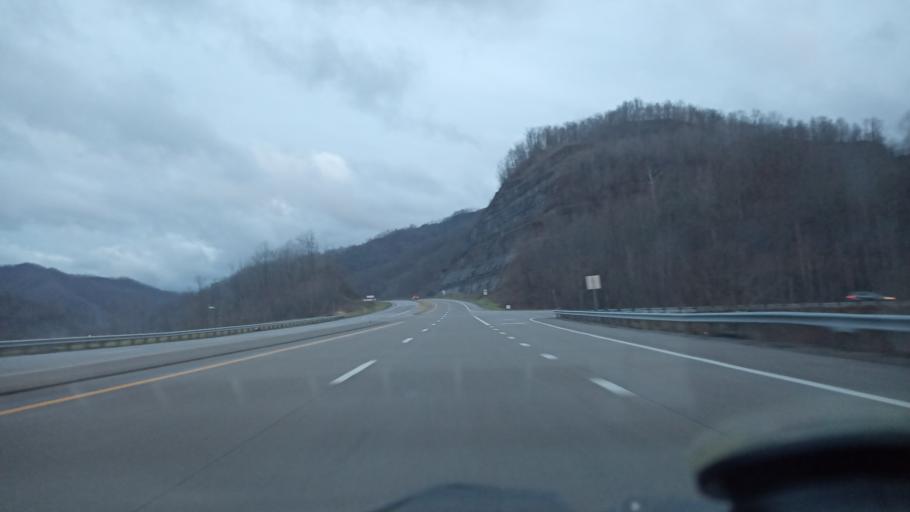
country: US
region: West Virginia
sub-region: Logan County
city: Mallory
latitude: 37.7690
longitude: -81.9227
